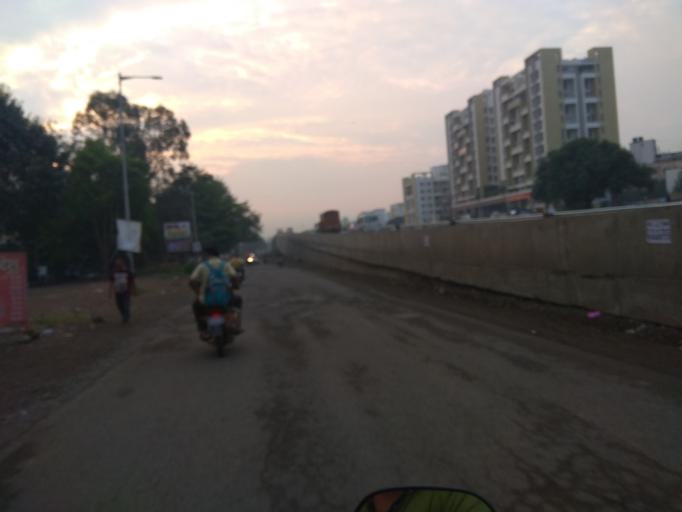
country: IN
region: Maharashtra
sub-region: Pune Division
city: Kharakvasla
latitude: 18.4865
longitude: 73.7972
